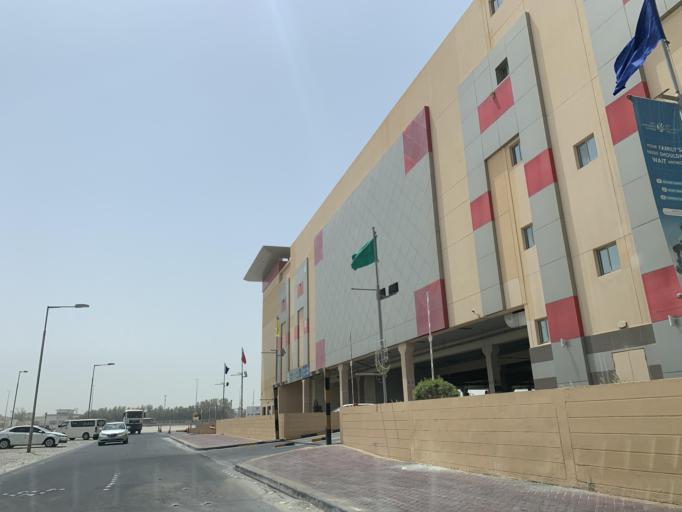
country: BH
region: Northern
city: Madinat `Isa
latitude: 26.1625
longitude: 50.5237
